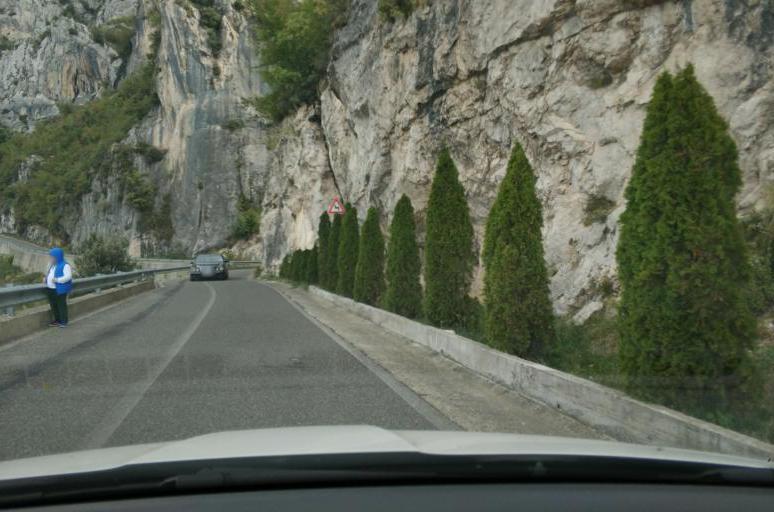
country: AL
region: Durres
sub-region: Rrethi i Krujes
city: Kruje
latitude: 41.5241
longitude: 19.7930
